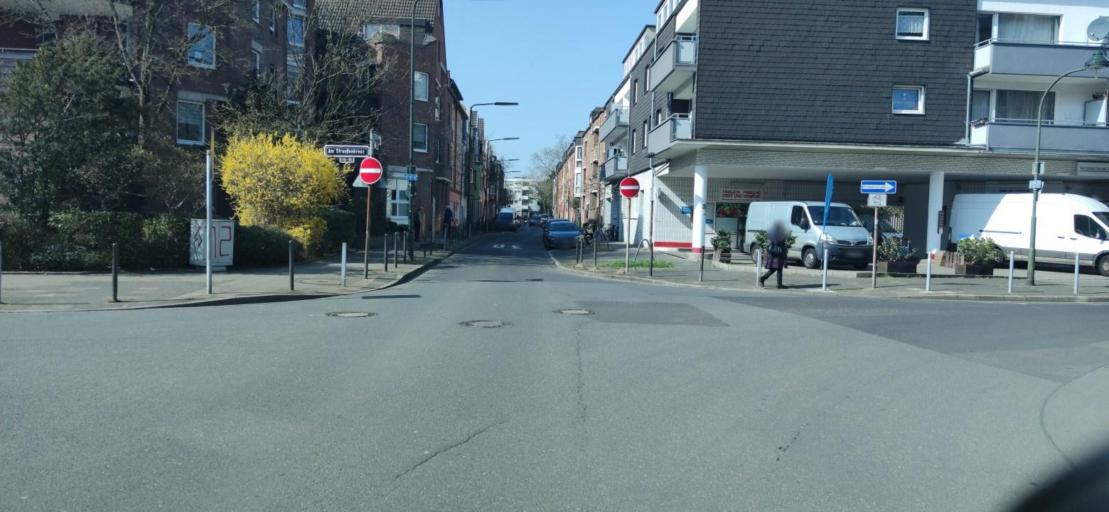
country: DE
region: North Rhine-Westphalia
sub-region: Regierungsbezirk Dusseldorf
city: Dusseldorf
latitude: 51.1941
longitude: 6.8362
